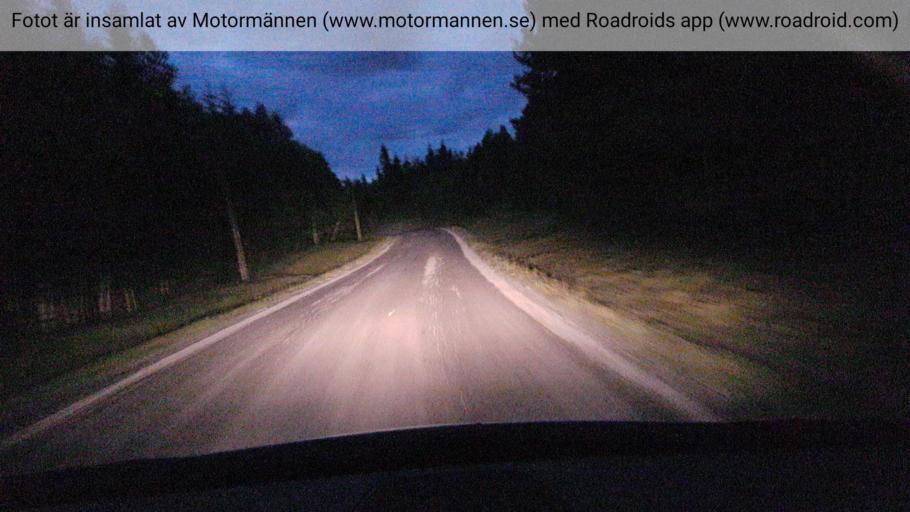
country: SE
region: Jaemtland
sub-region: OEstersunds Kommun
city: Lit
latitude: 63.3216
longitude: 15.2202
